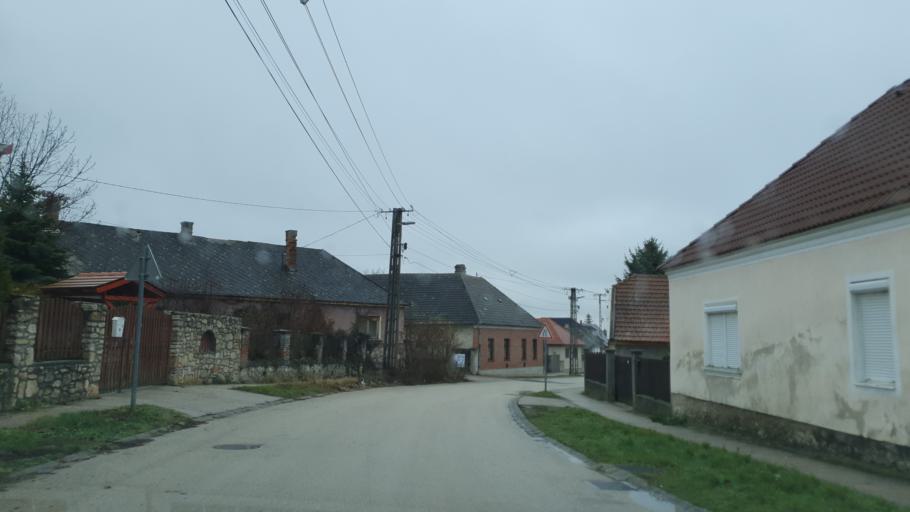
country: HU
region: Veszprem
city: Veszprem
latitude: 47.1440
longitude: 17.9457
